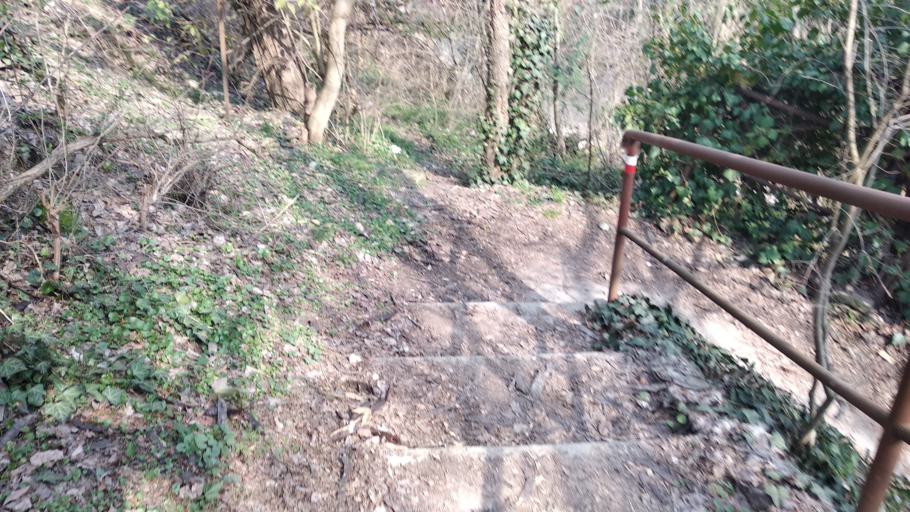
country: IT
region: Emilia-Romagna
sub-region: Provincia di Bologna
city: Ponticella
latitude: 44.4584
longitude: 11.3740
